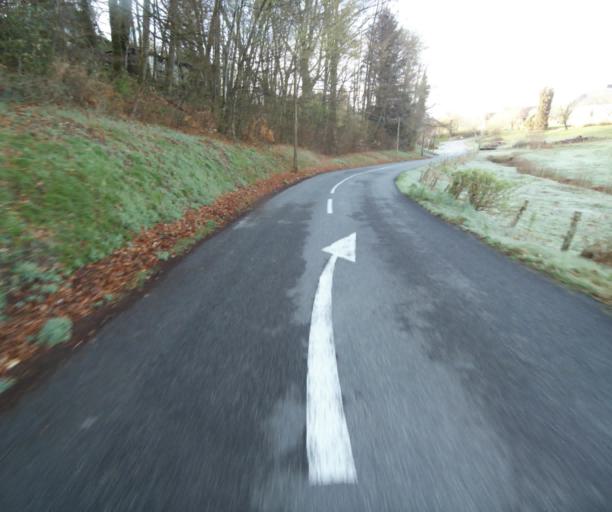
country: FR
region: Limousin
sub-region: Departement de la Correze
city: Naves
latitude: 45.3048
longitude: 1.8409
